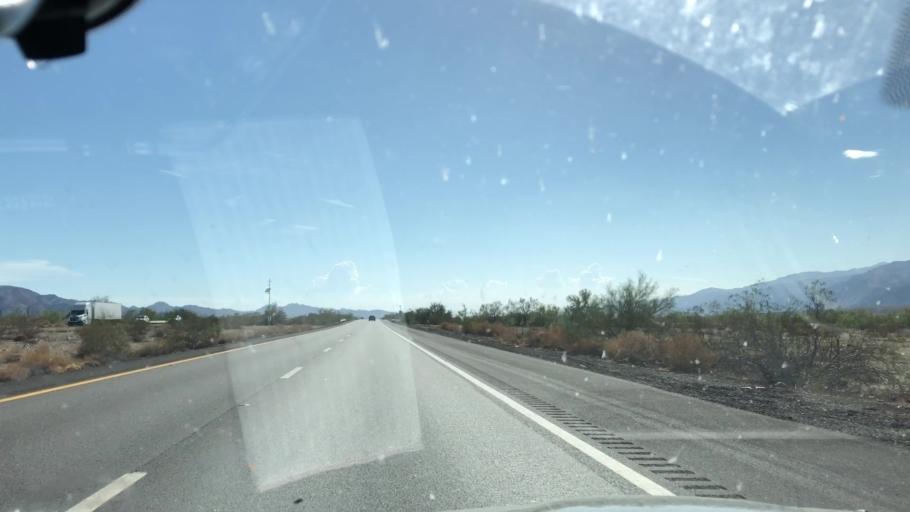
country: US
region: California
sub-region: Imperial County
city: Niland
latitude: 33.6881
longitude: -115.5180
